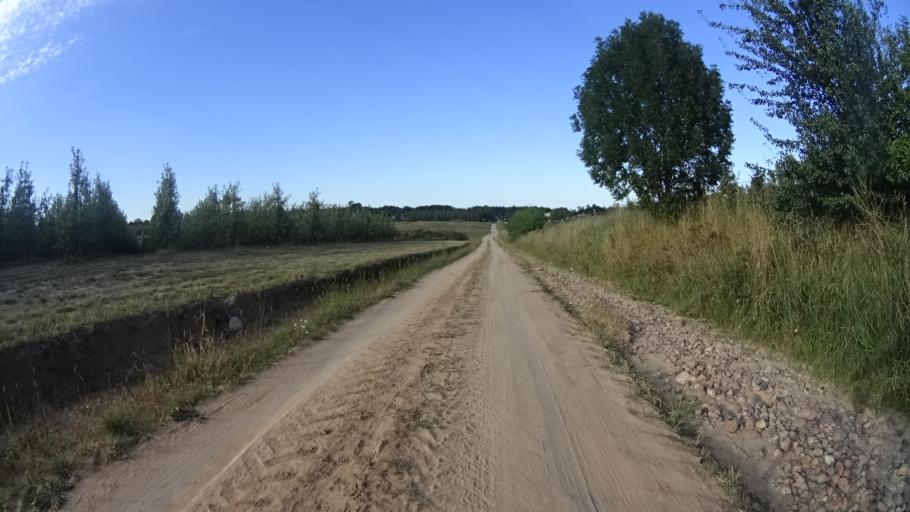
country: PL
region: Masovian Voivodeship
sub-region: Powiat grojecki
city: Goszczyn
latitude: 51.6898
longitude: 20.8136
